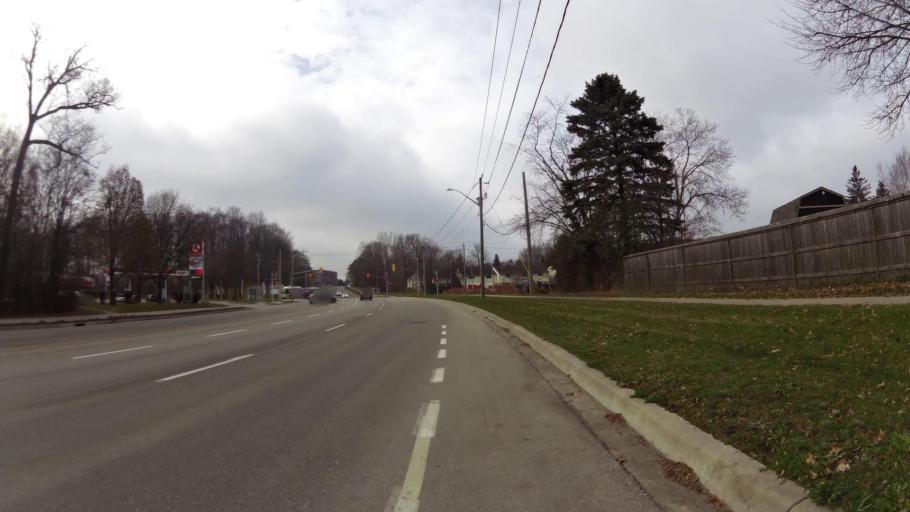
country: CA
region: Ontario
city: Kitchener
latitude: 43.4165
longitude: -80.4790
